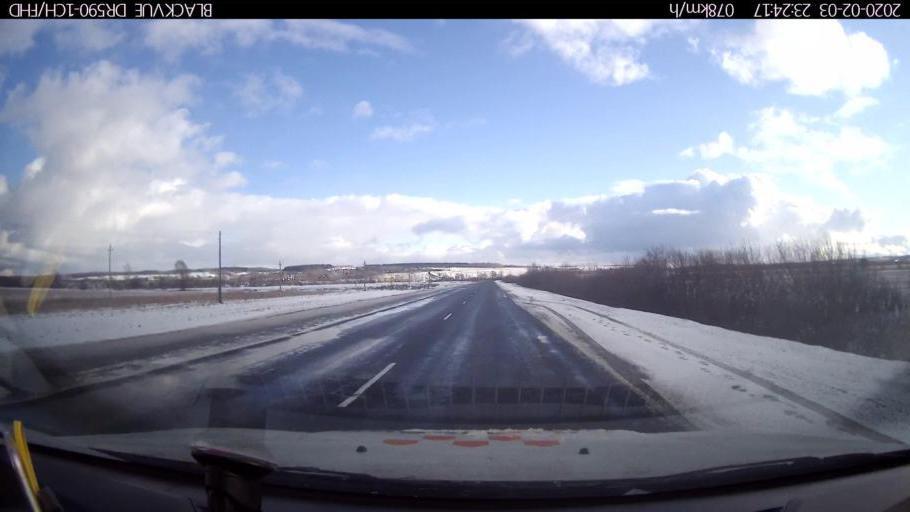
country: RU
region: Nizjnij Novgorod
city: Kstovo
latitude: 56.0135
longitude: 44.1979
